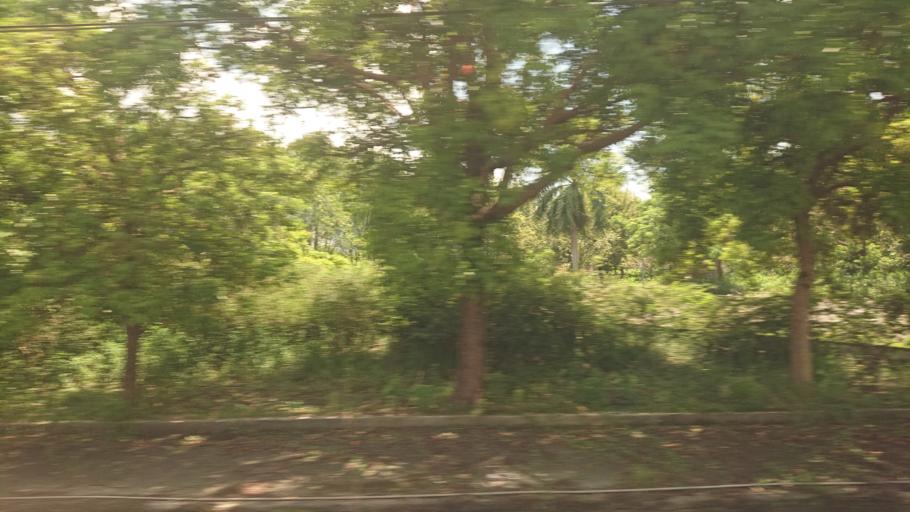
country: TW
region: Taiwan
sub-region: Nantou
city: Puli
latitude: 23.9852
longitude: 120.9590
